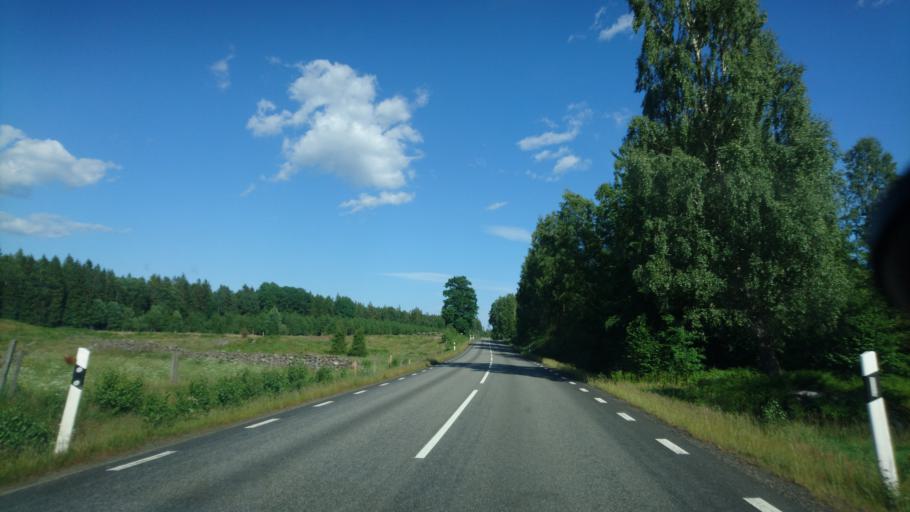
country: SE
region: Skane
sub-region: Osby Kommun
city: Lonsboda
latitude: 56.3912
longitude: 14.3937
